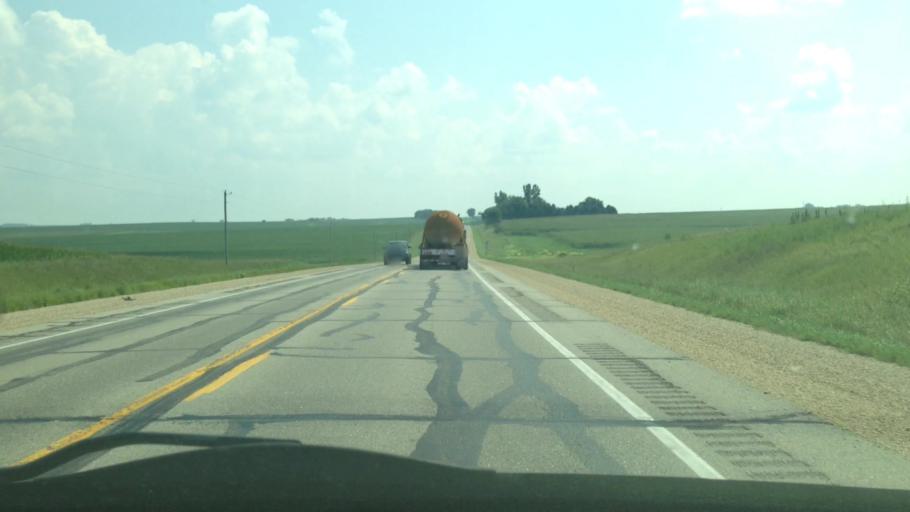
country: US
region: Iowa
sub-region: Chickasaw County
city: New Hampton
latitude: 43.1919
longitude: -92.2982
